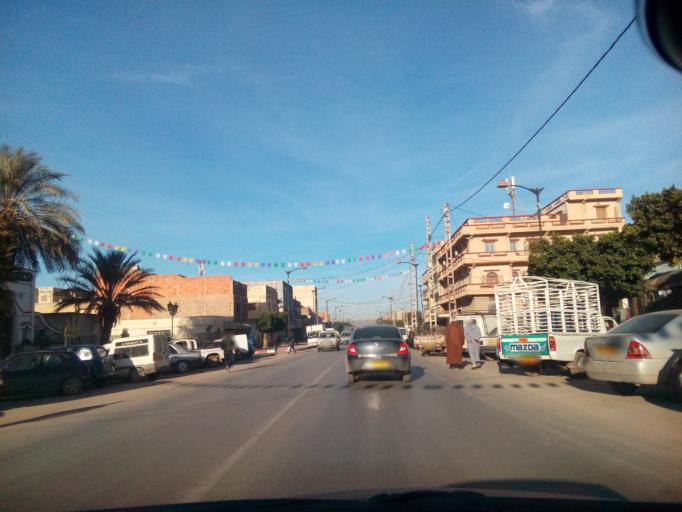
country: DZ
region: Mostaganem
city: Mostaganem
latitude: 35.7804
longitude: 0.1880
